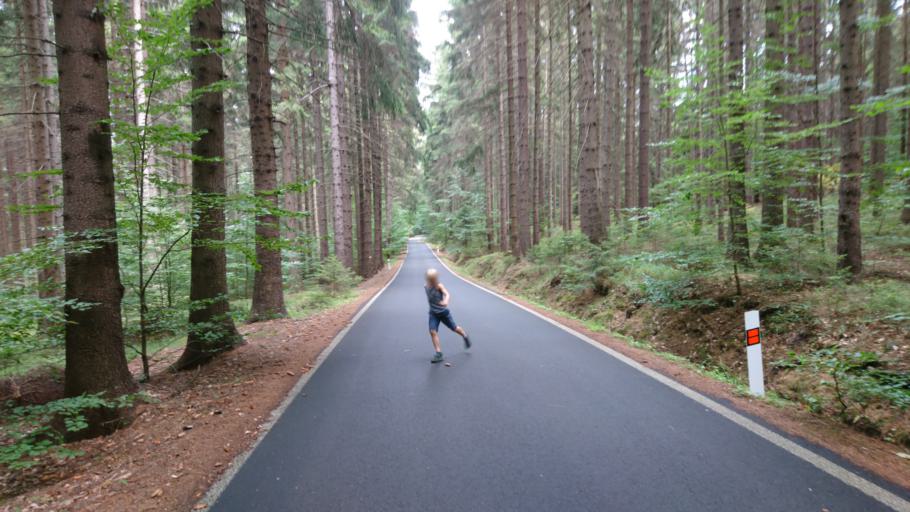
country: CZ
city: Novy Bor
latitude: 50.7929
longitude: 14.5663
